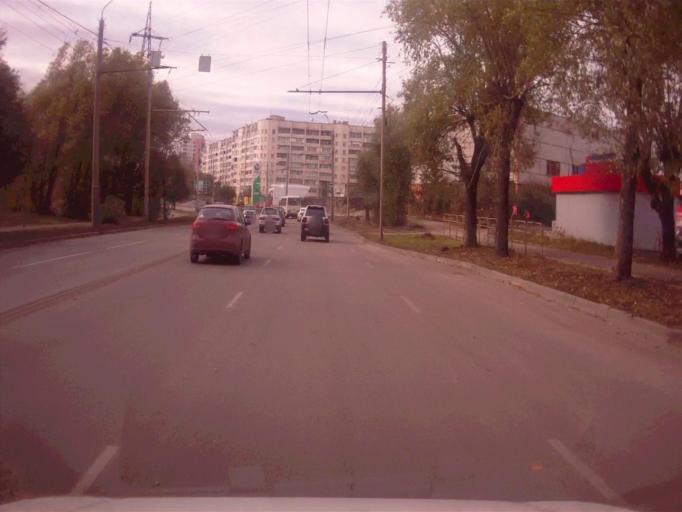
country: RU
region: Chelyabinsk
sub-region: Gorod Chelyabinsk
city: Chelyabinsk
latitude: 55.1164
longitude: 61.4444
